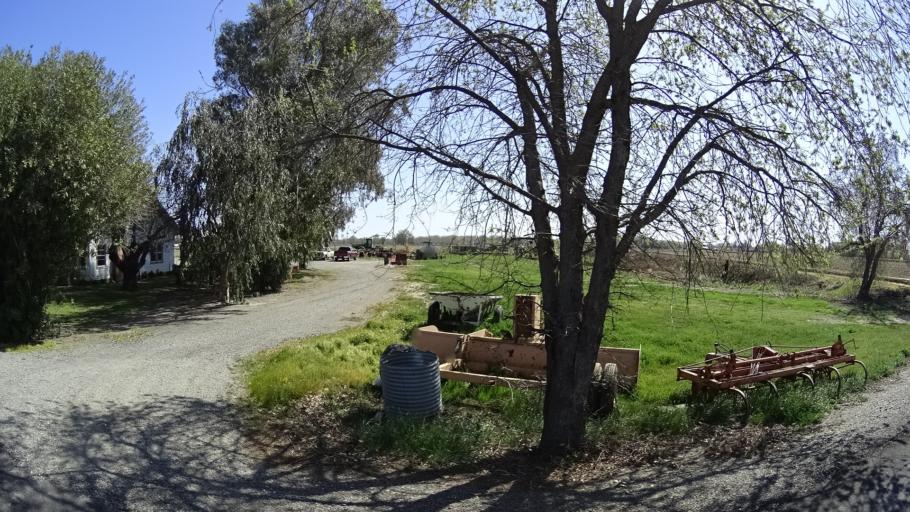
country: US
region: California
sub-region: Glenn County
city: Willows
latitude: 39.4534
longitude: -122.0314
